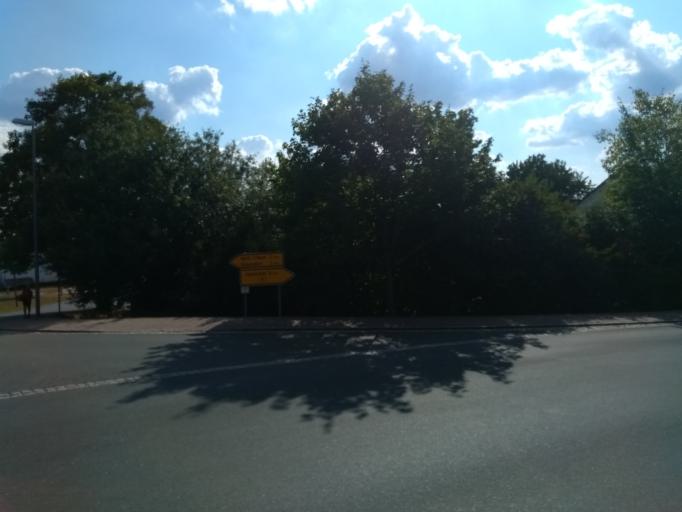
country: DE
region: Bavaria
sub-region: Regierungsbezirk Mittelfranken
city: Hagenbuchach
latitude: 49.5345
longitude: 10.7714
